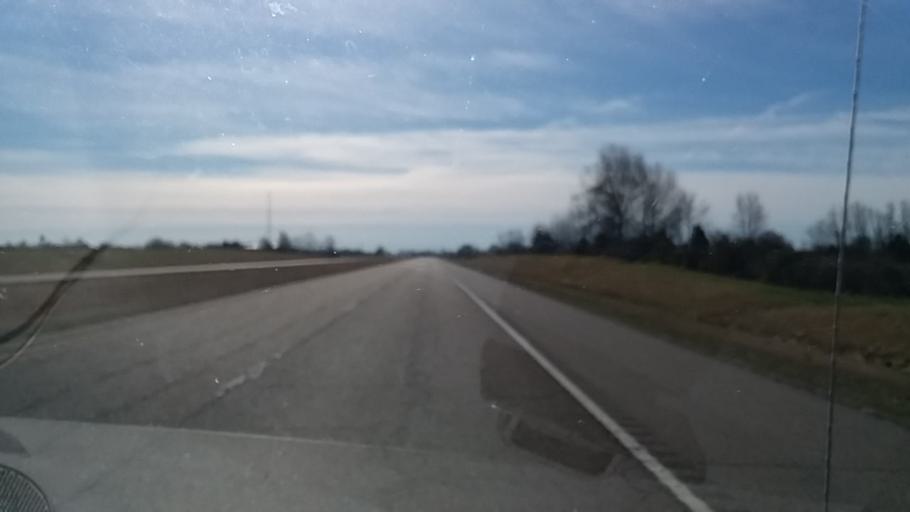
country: US
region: Tennessee
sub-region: Crockett County
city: Alamo
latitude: 35.7865
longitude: -89.1496
